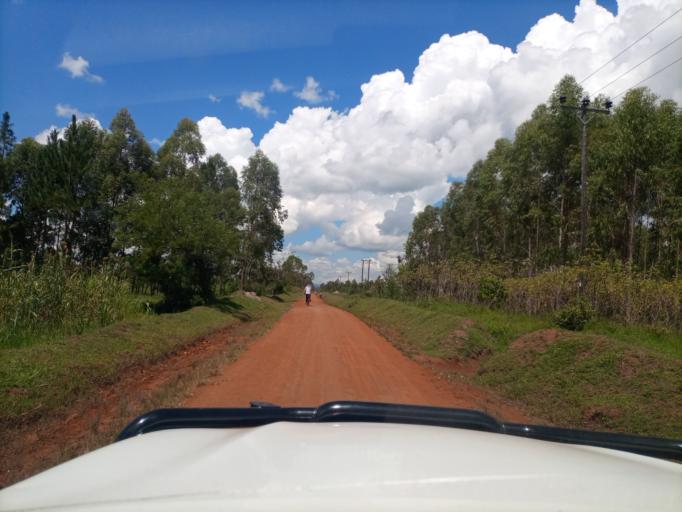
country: UG
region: Eastern Region
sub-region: Tororo District
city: Tororo
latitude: 0.6653
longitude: 34.0021
